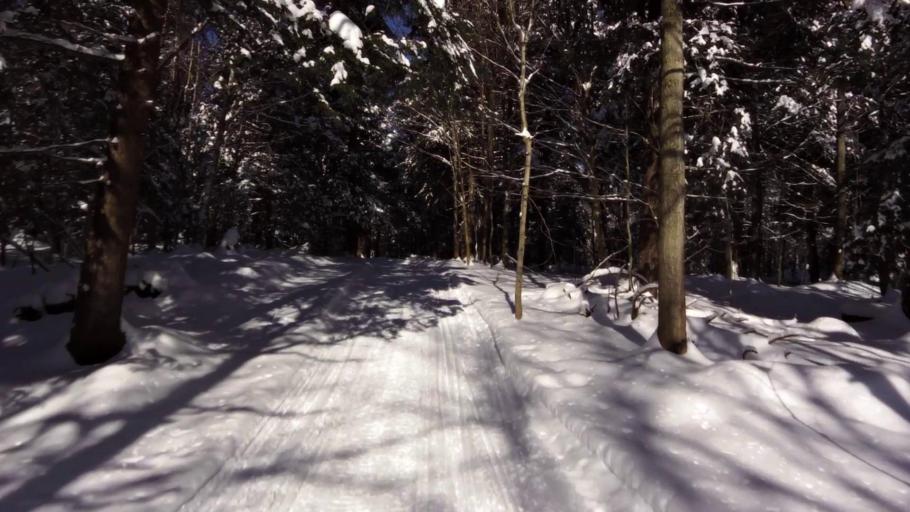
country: US
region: New York
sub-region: Chautauqua County
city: Silver Creek
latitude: 42.3736
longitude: -79.1552
